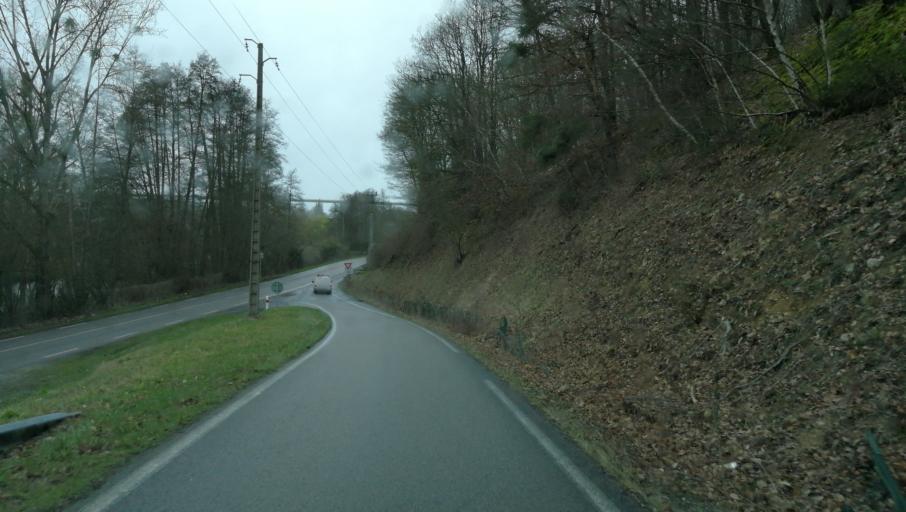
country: FR
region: Haute-Normandie
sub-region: Departement de l'Eure
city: Nassandres
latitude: 49.1537
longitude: 0.7298
